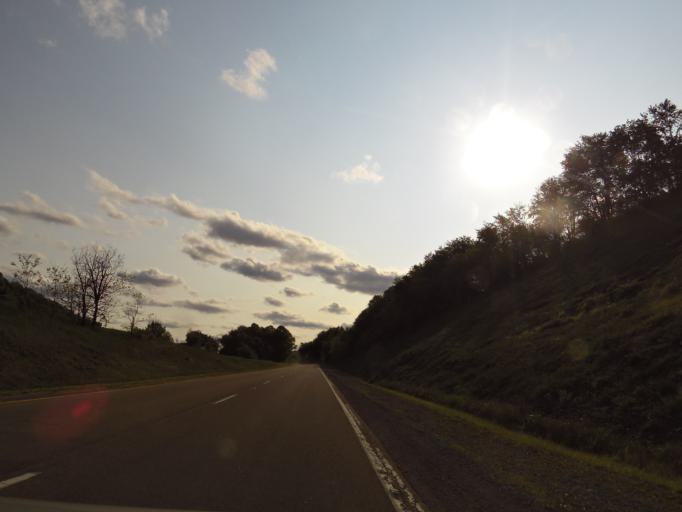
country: US
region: Virginia
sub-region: Tazewell County
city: Tazewell
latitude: 37.1466
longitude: -81.4999
